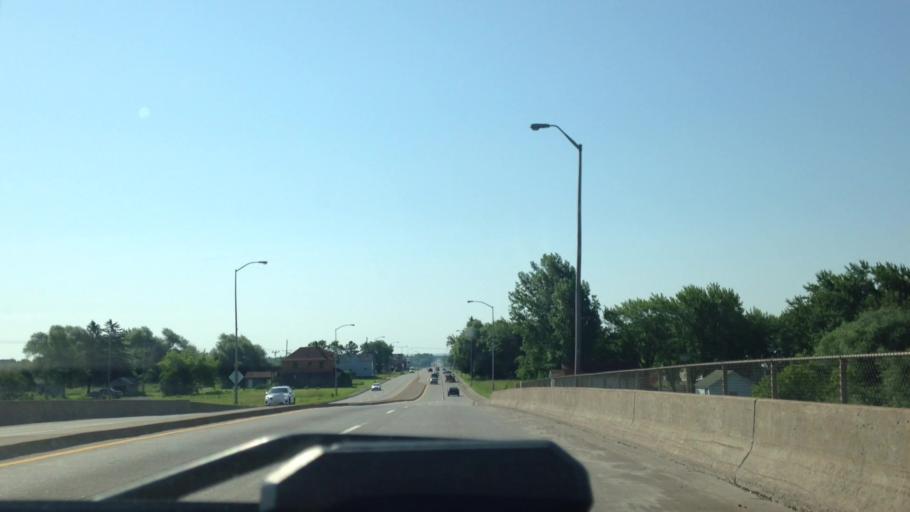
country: US
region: Wisconsin
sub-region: Douglas County
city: Superior
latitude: 46.7036
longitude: -92.0435
